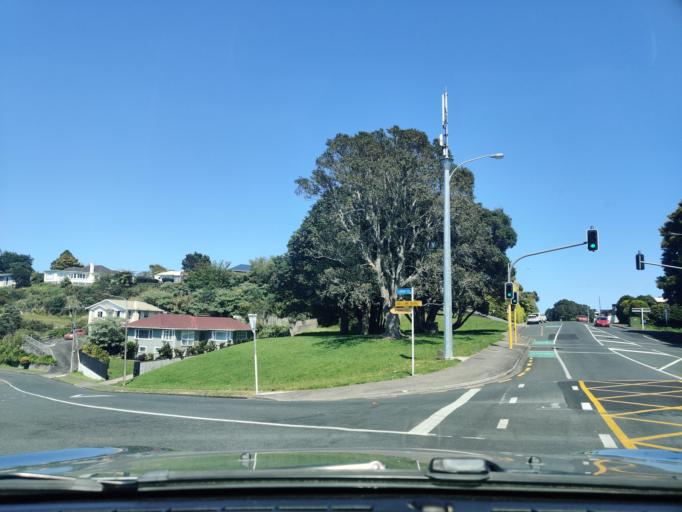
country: NZ
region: Taranaki
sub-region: New Plymouth District
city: New Plymouth
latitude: -39.0638
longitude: 174.0543
